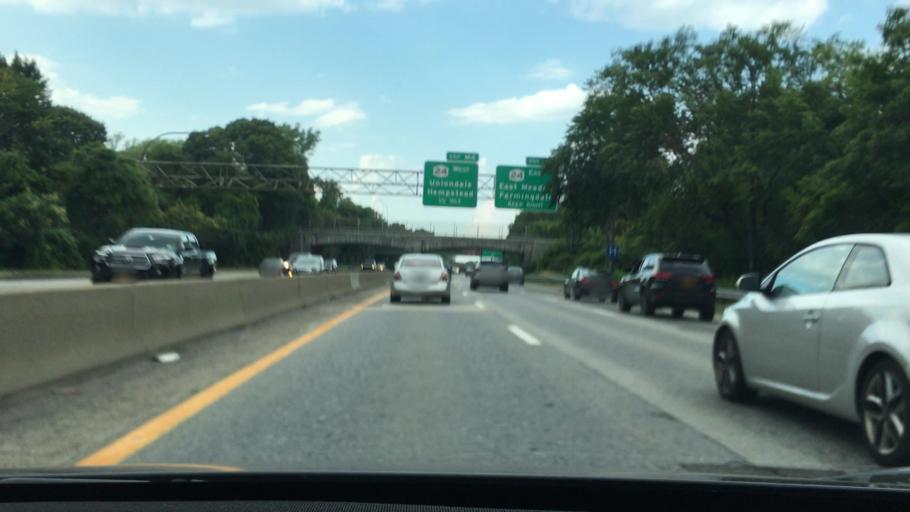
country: US
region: New York
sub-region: Nassau County
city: Uniondale
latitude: 40.7161
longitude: -73.5805
